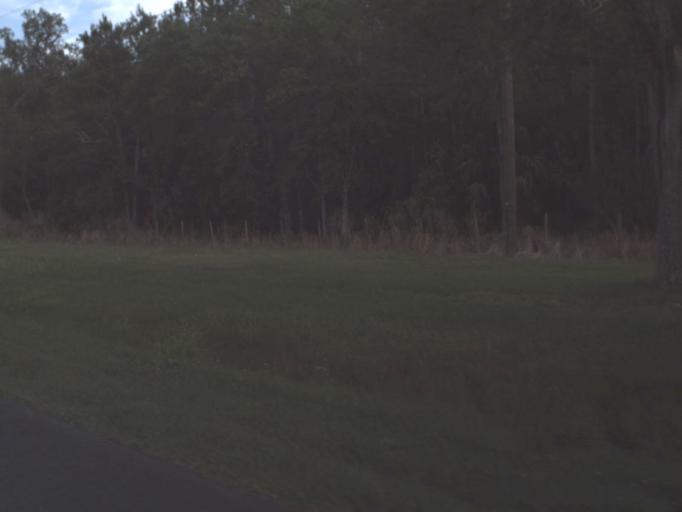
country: US
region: Florida
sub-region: Marion County
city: Silver Springs Shores
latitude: 29.2181
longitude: -82.0171
